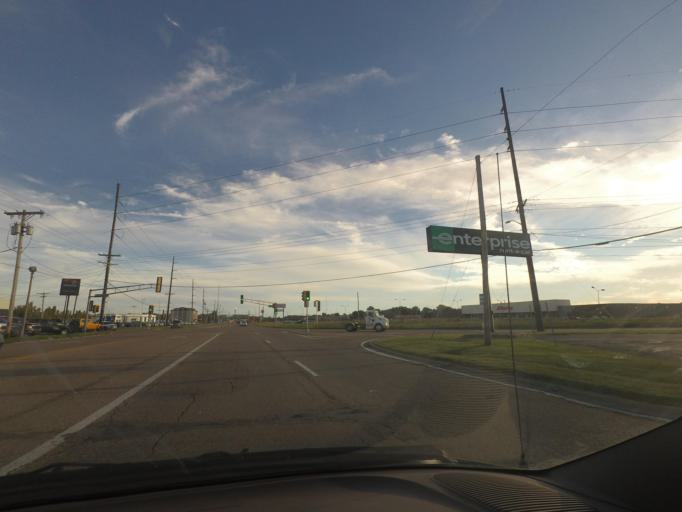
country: US
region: Illinois
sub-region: Sangamon County
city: Grandview
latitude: 39.7908
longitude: -89.6060
